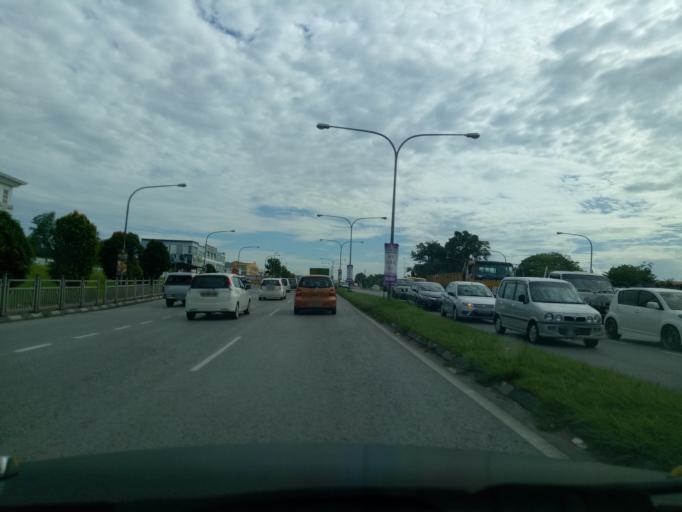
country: MY
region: Sarawak
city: Kuching
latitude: 1.4697
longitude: 110.3283
